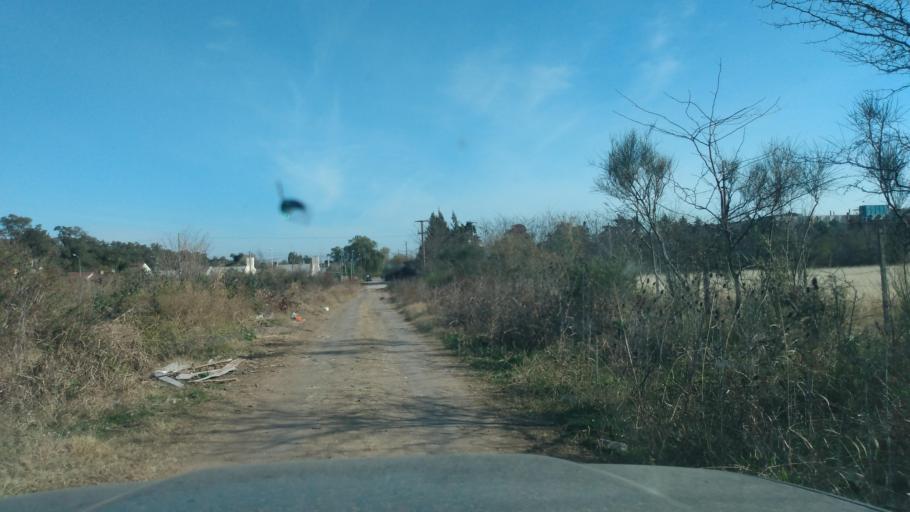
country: AR
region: Buenos Aires
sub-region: Partido de Lujan
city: Lujan
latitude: -34.5659
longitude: -59.1390
